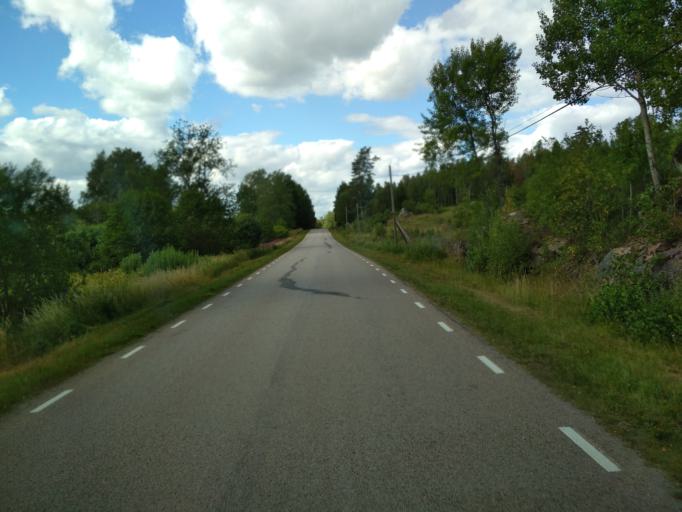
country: SE
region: Uppsala
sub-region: Enkopings Kommun
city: Orsundsbro
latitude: 59.7777
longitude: 17.2131
